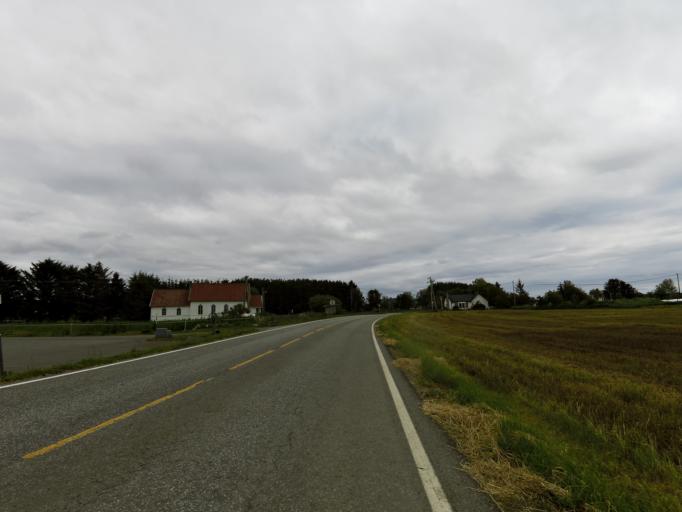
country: NO
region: Vest-Agder
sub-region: Farsund
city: Vestbygd
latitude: 58.1167
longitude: 6.6040
